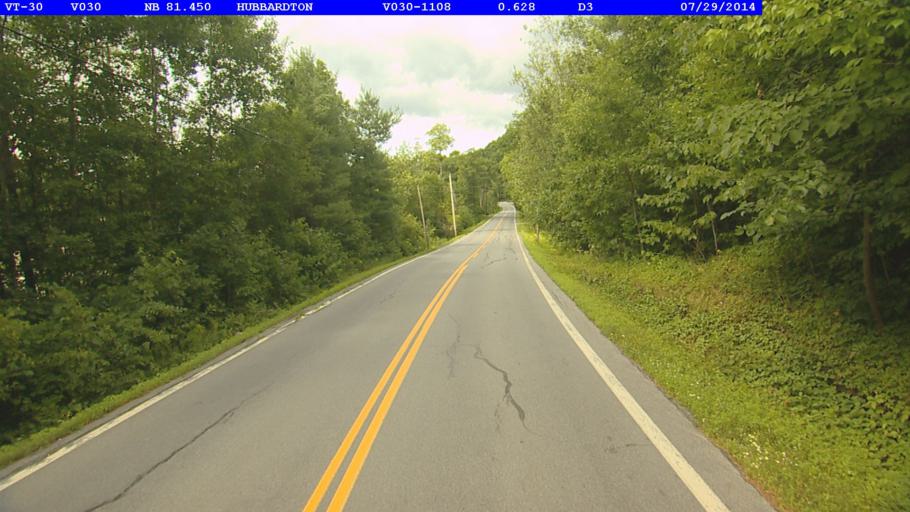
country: US
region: Vermont
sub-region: Rutland County
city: Castleton
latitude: 43.6877
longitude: -73.1862
